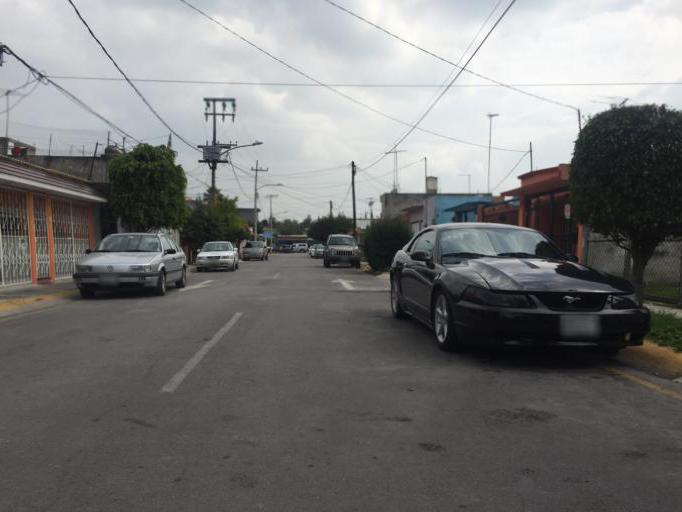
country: MX
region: Mexico
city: Cuautitlan Izcalli
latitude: 19.6591
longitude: -99.2170
